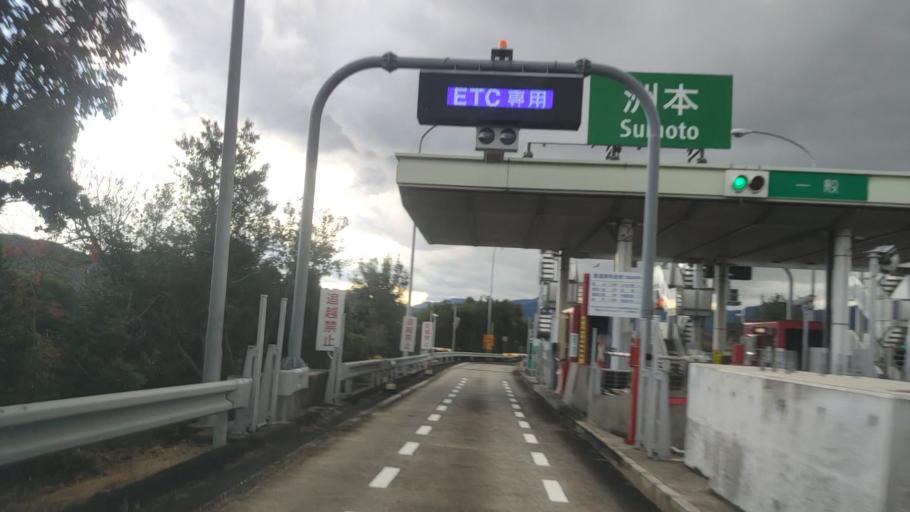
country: JP
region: Hyogo
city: Sumoto
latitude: 34.3427
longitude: 134.8478
